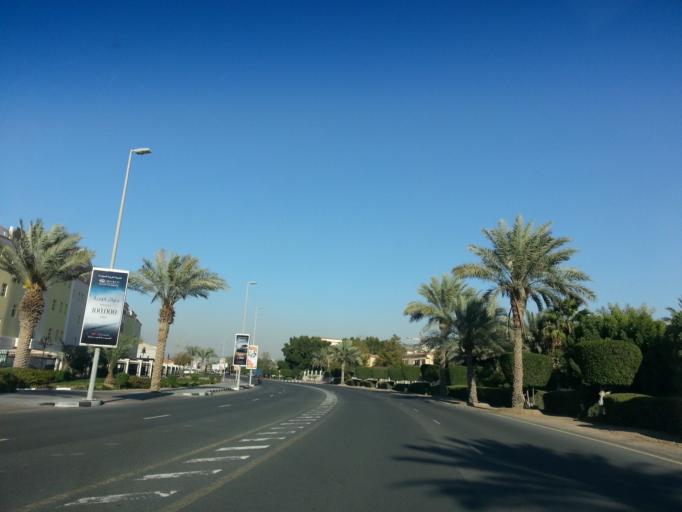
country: AE
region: Dubai
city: Dubai
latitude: 25.0013
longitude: 55.1626
